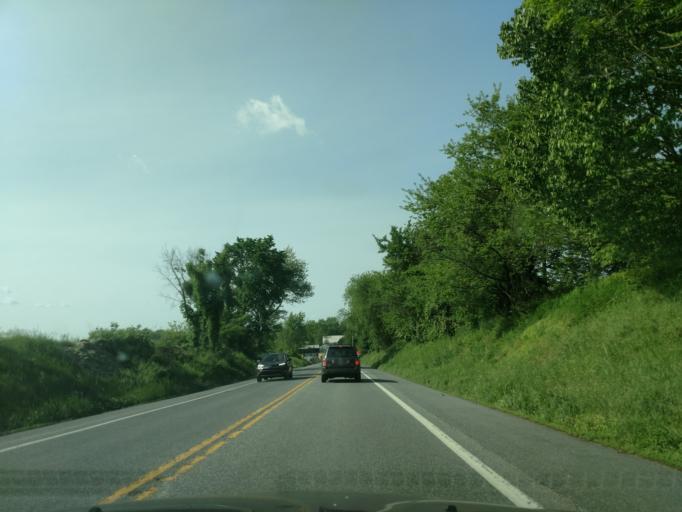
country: US
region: Pennsylvania
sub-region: Lebanon County
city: Cornwall
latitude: 40.2960
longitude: -76.4246
